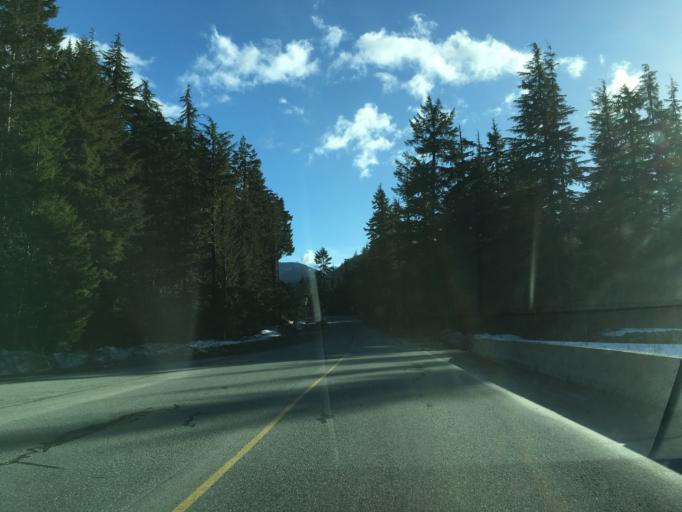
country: CA
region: British Columbia
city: Whistler
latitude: 50.0842
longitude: -123.0373
